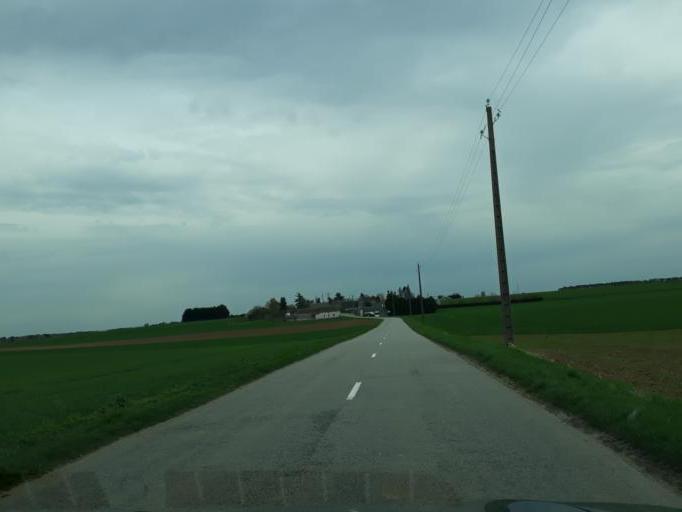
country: FR
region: Centre
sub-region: Departement du Loiret
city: Epieds-en-Beauce
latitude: 47.9222
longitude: 1.5889
